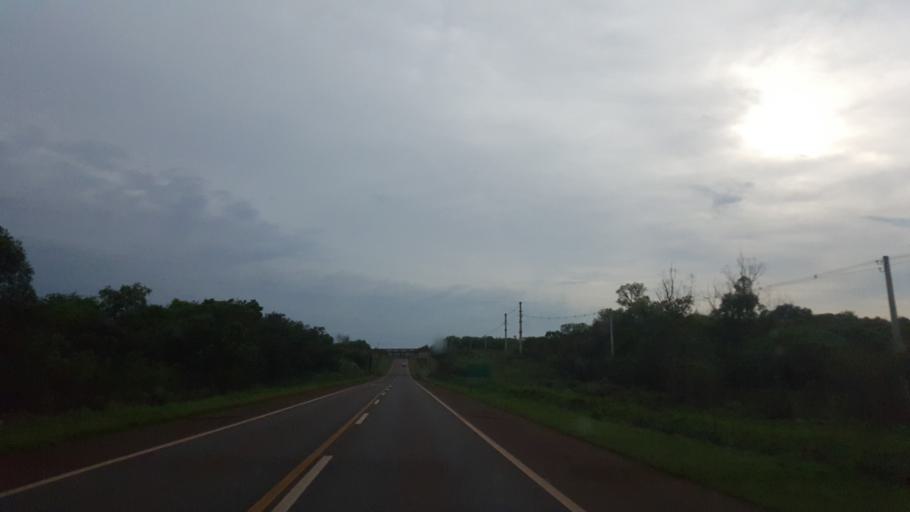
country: AR
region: Misiones
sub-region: Departamento de Apostoles
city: San Jose
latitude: -27.7643
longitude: -55.7981
